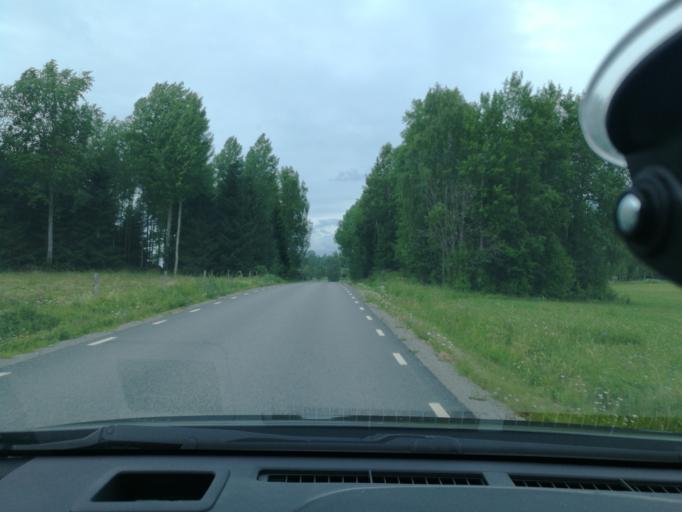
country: SE
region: Vaestmanland
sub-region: Surahammars Kommun
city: Ramnas
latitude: 59.8368
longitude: 16.3146
